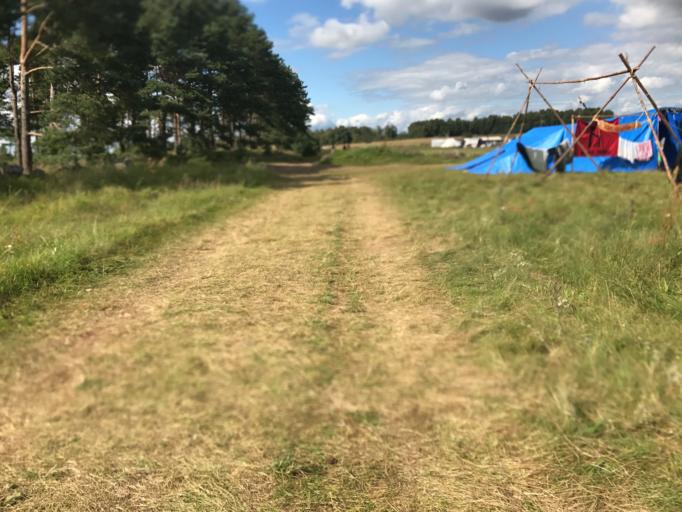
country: SE
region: Skane
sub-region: Kristianstads Kommun
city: Fjalkinge
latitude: 56.0080
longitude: 14.3025
